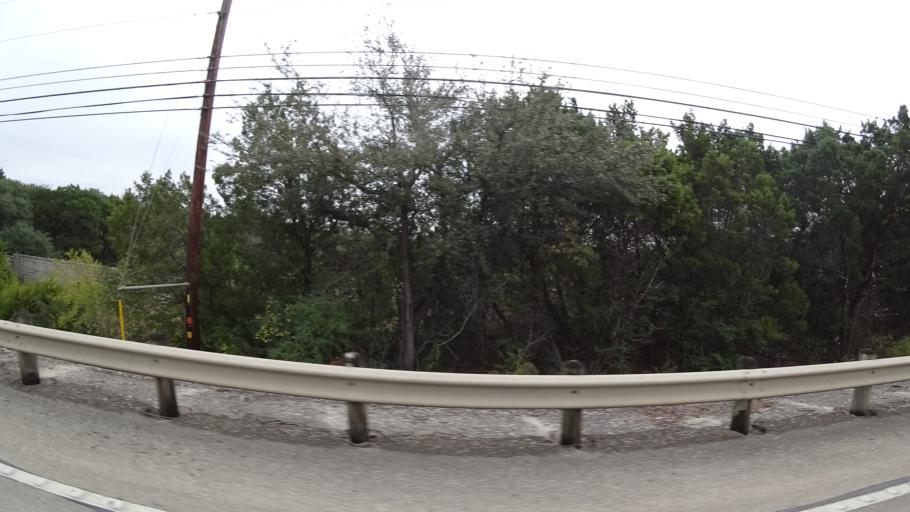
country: US
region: Texas
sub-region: Travis County
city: Barton Creek
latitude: 30.2264
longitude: -97.8898
